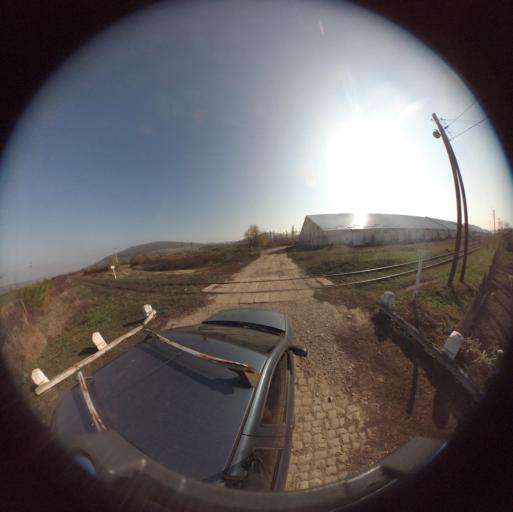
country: RO
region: Vaslui
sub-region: Comuna Dumesti
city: Dumesti
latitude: 46.8311
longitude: 27.2647
